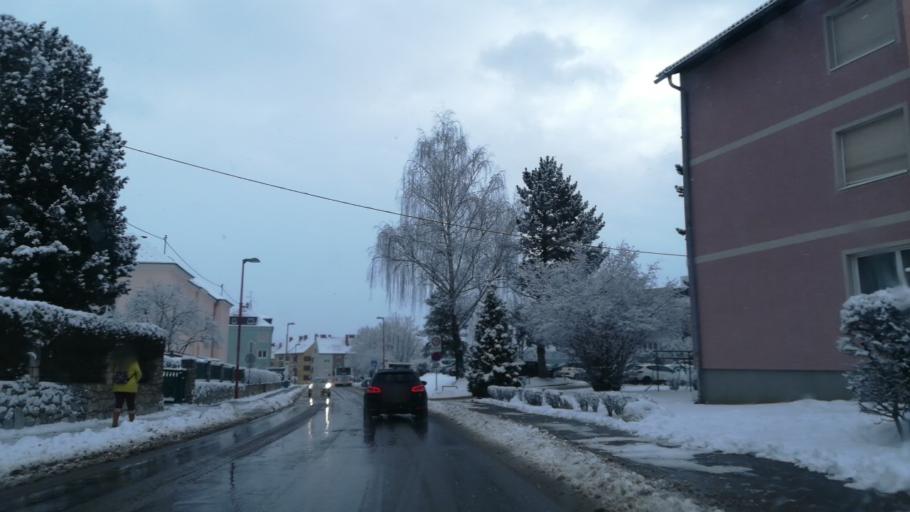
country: AT
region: Styria
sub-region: Politischer Bezirk Murtal
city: Fohnsdorf
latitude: 47.2059
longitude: 14.6636
